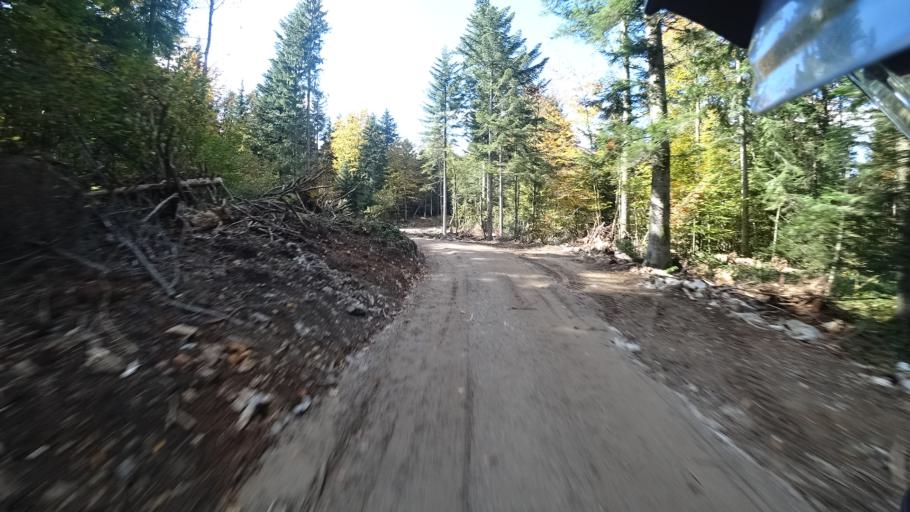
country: HR
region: Karlovacka
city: Plaski
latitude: 45.0603
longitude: 15.3504
